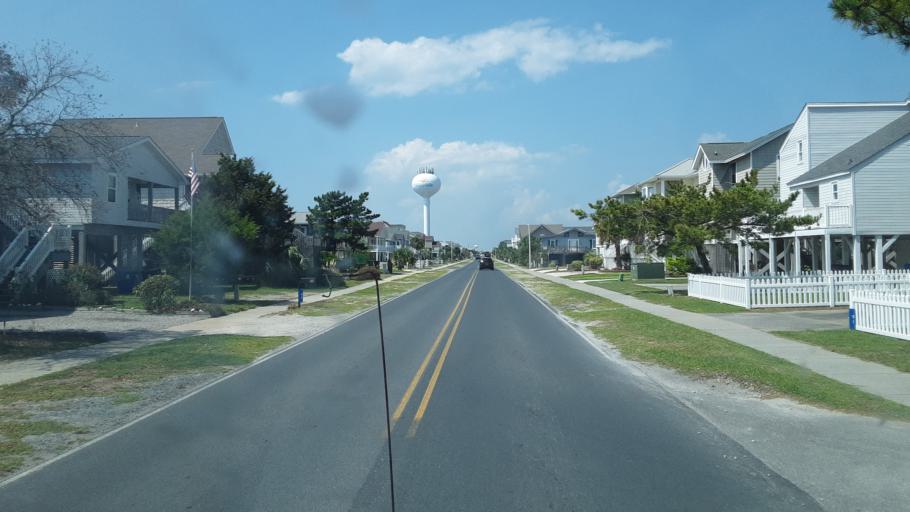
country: US
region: North Carolina
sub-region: Brunswick County
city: Sunset Beach
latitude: 33.8904
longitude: -78.4285
